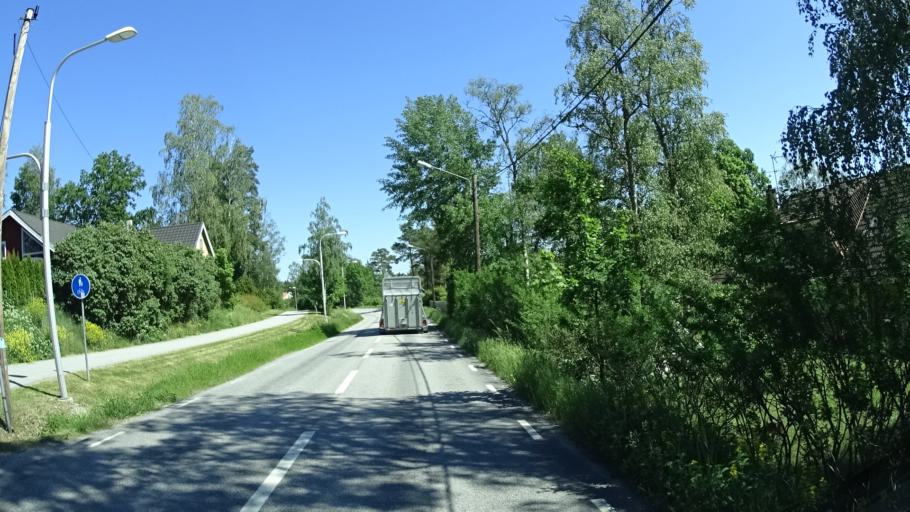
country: SE
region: Stockholm
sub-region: Vallentuna Kommun
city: Vallentuna
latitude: 59.5818
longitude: 18.1021
